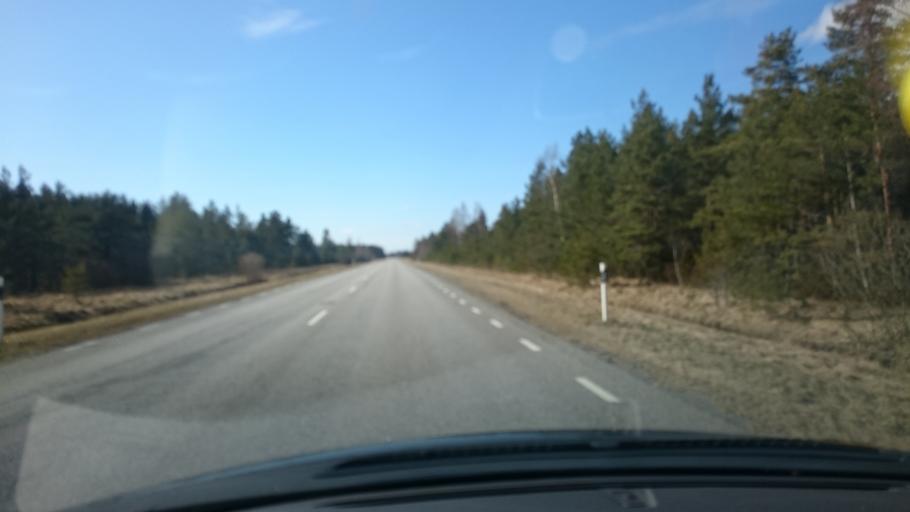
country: EE
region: Laeaene
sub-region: Lihula vald
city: Lihula
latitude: 58.6140
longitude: 23.9191
